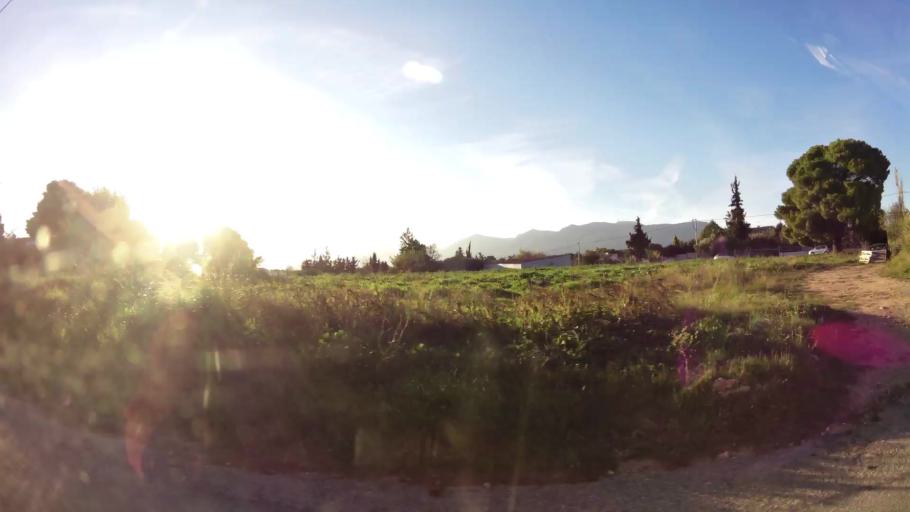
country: GR
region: Attica
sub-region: Nomarchia Anatolikis Attikis
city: Kryoneri
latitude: 38.1261
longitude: 23.8301
